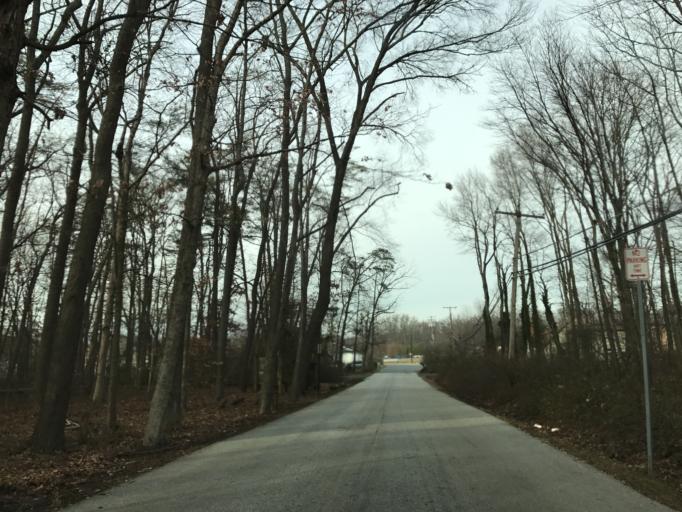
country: US
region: Maryland
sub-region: Baltimore County
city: White Marsh
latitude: 39.3880
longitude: -76.4142
